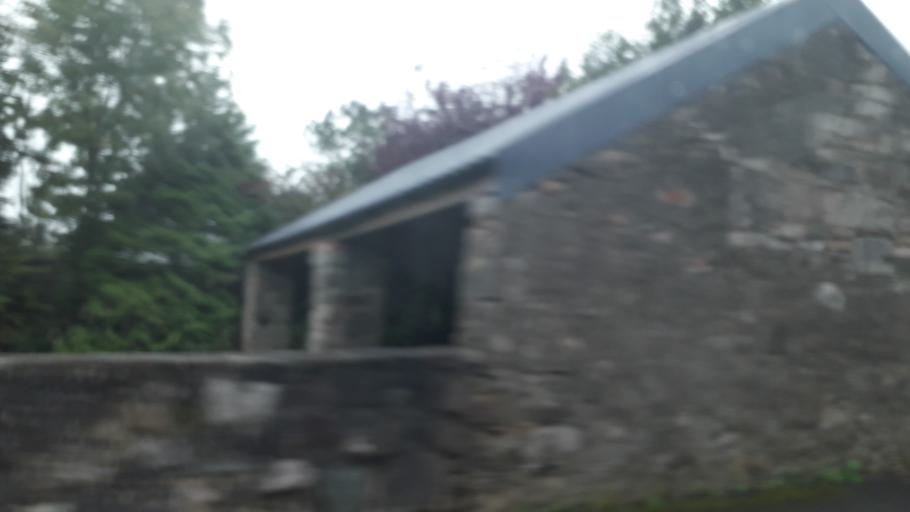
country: IE
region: Leinster
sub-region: An Longfort
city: Longford
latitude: 53.7411
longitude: -7.8022
